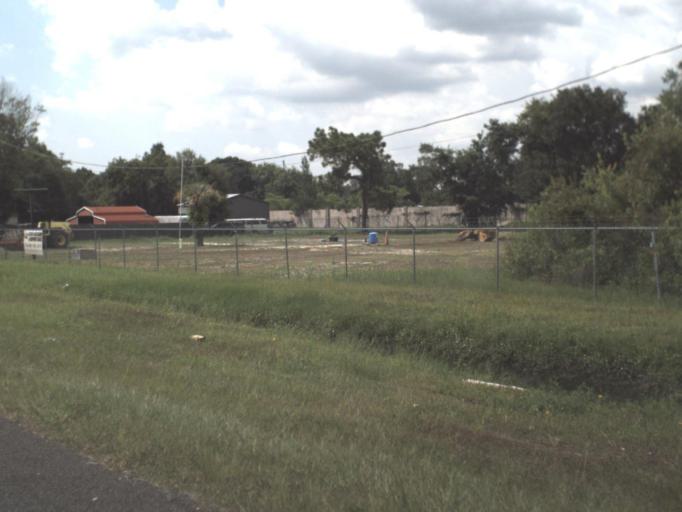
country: US
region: Florida
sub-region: Pasco County
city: Land O' Lakes
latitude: 28.2526
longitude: -82.4682
